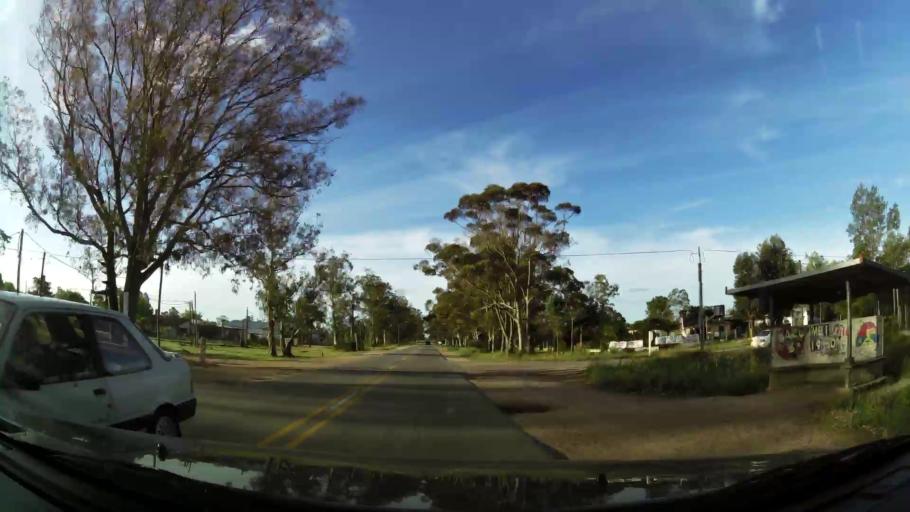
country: UY
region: Canelones
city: Atlantida
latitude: -34.7687
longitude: -55.8419
